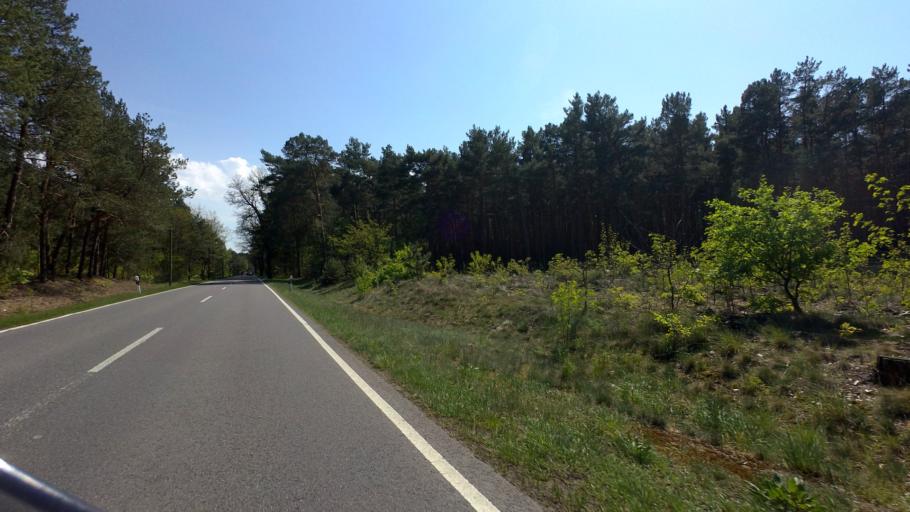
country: DE
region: Brandenburg
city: Lieberose
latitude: 52.0033
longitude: 14.1963
